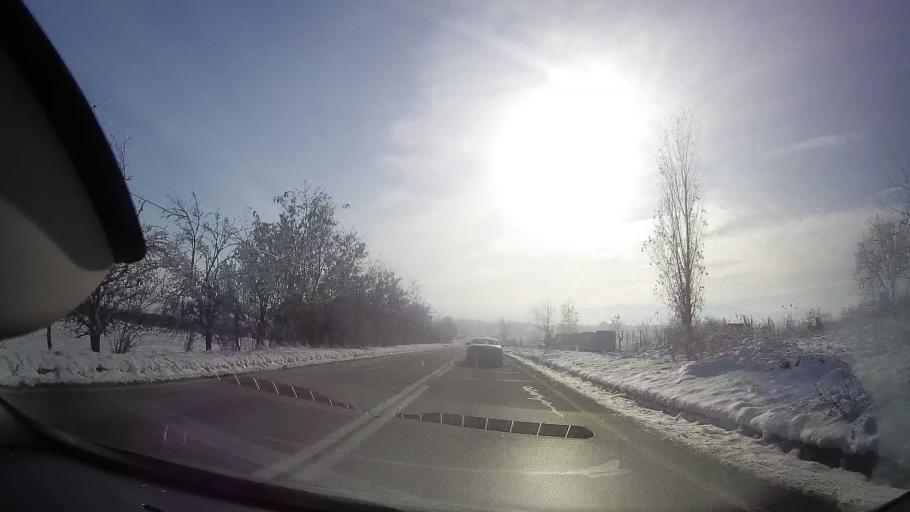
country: RO
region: Neamt
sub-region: Comuna Dobreni
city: Dobreni
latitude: 47.0074
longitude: 26.4245
